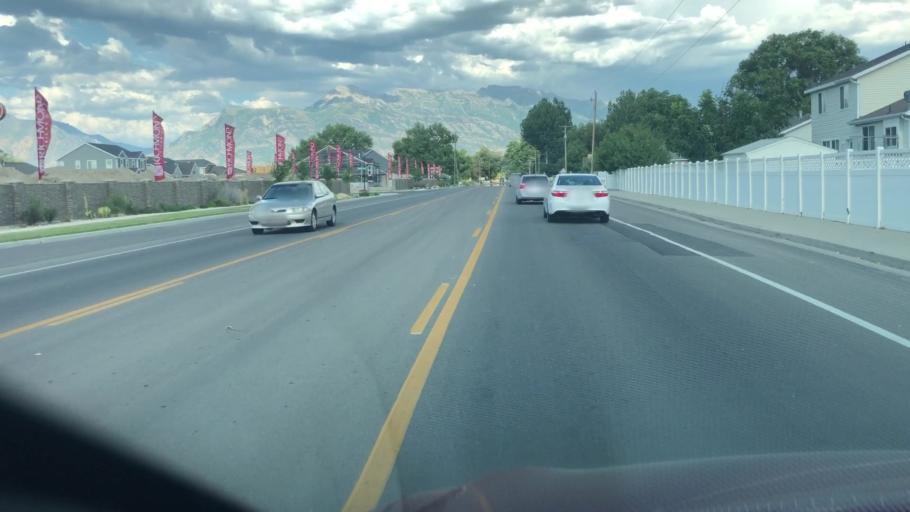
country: US
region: Utah
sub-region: Utah County
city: Lehi
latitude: 40.3872
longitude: -111.8700
